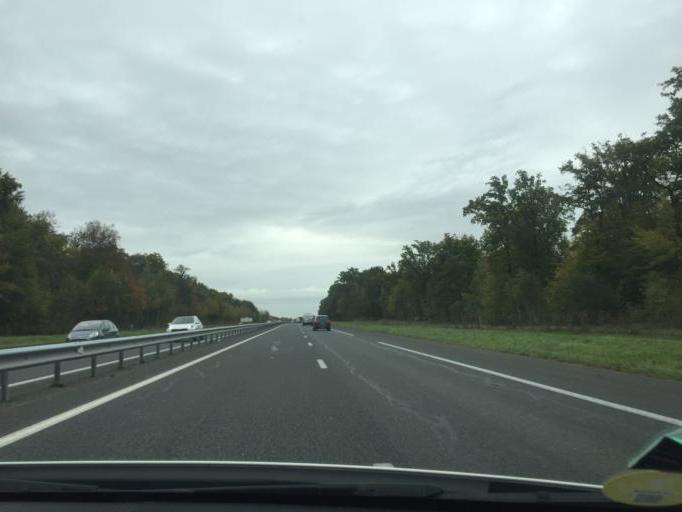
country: FR
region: Bourgogne
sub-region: Departement de l'Yonne
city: Egriselles-le-Bocage
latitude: 48.1332
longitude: 3.1512
